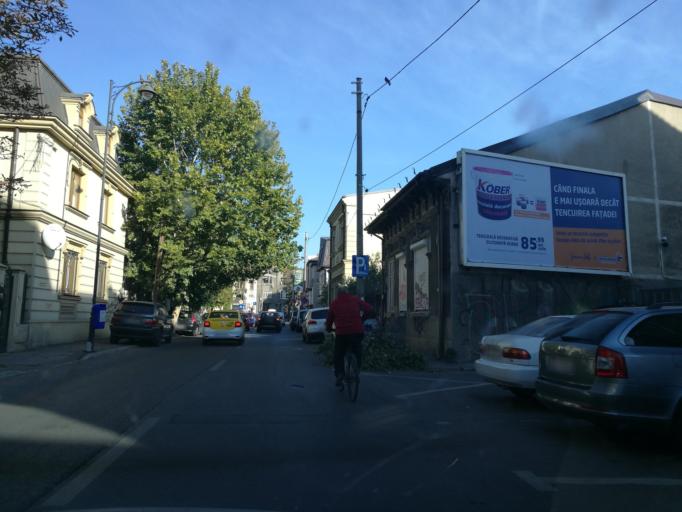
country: RO
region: Bucuresti
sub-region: Municipiul Bucuresti
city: Bucharest
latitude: 44.4423
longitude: 26.1084
